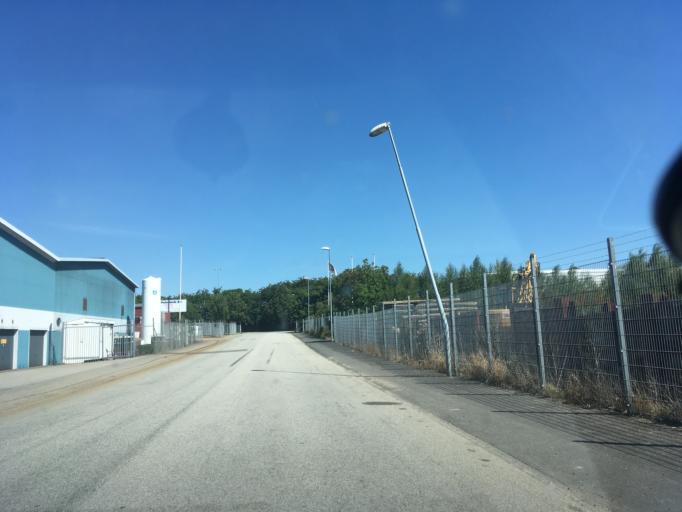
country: SE
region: Skane
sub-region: Trelleborgs Kommun
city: Trelleborg
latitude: 55.3841
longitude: 13.1429
